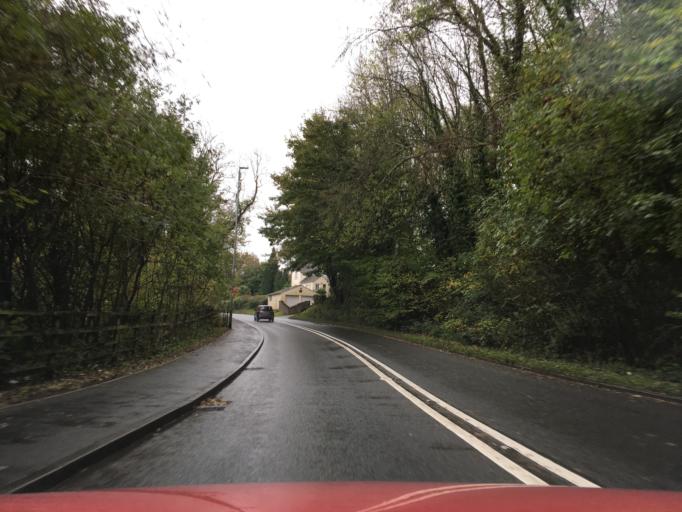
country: GB
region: Wales
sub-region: Newport
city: Caerleon
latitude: 51.6018
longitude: -2.9620
